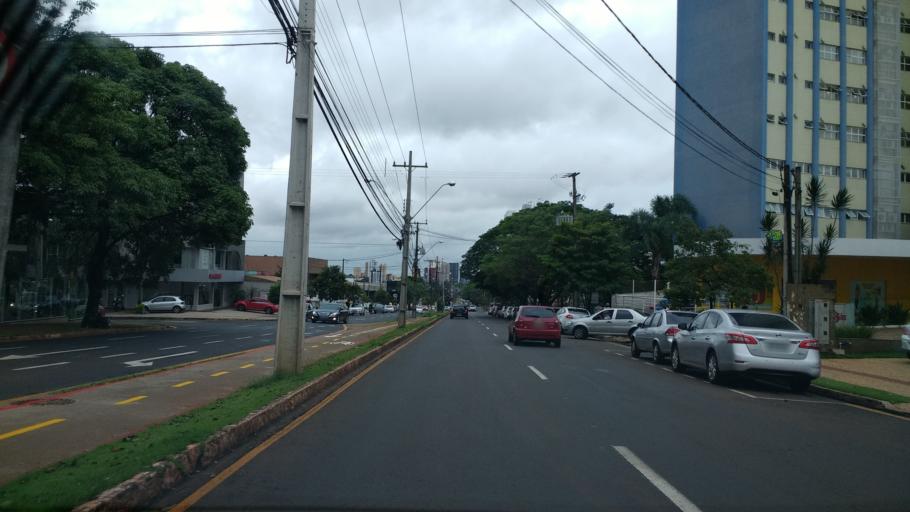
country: BR
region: Parana
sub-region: Londrina
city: Londrina
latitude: -23.3348
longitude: -51.1737
